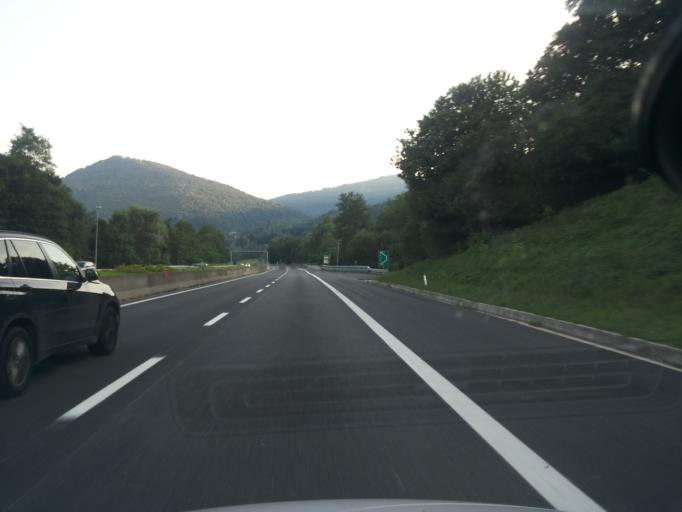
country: IT
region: Piedmont
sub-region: Provincia Verbano-Cusio-Ossola
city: Brovello
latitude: 45.8559
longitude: 8.5370
